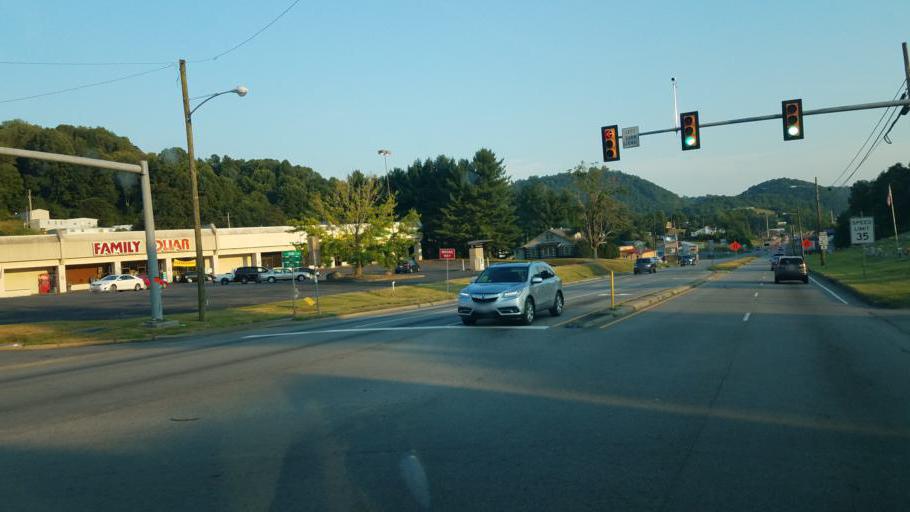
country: US
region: Virginia
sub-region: Scott County
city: Weber City
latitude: 36.6168
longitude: -82.5680
